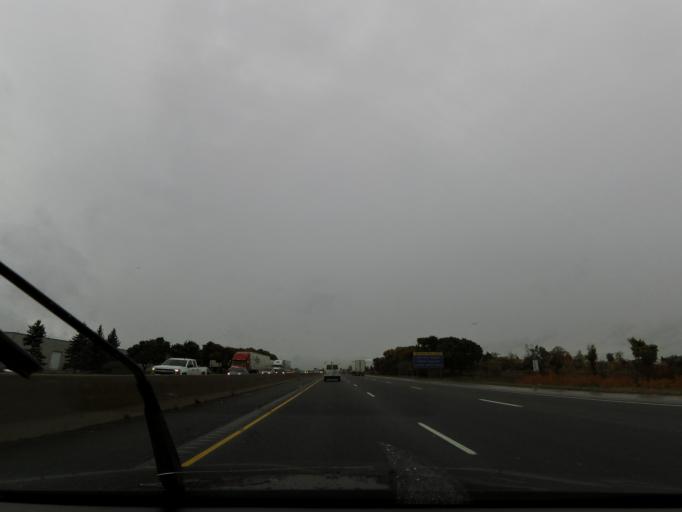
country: CA
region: Ontario
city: Cambridge
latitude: 43.4147
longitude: -80.3088
